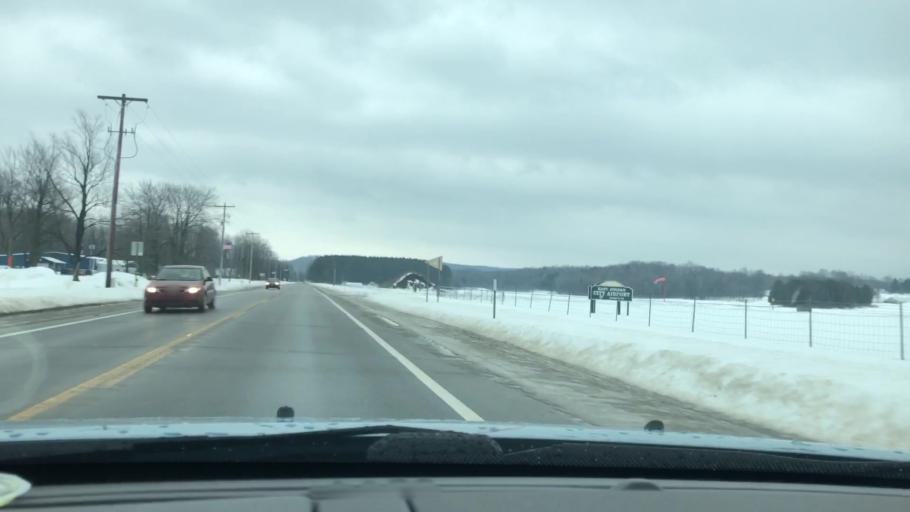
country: US
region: Michigan
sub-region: Charlevoix County
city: East Jordan
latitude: 45.1325
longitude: -85.1072
